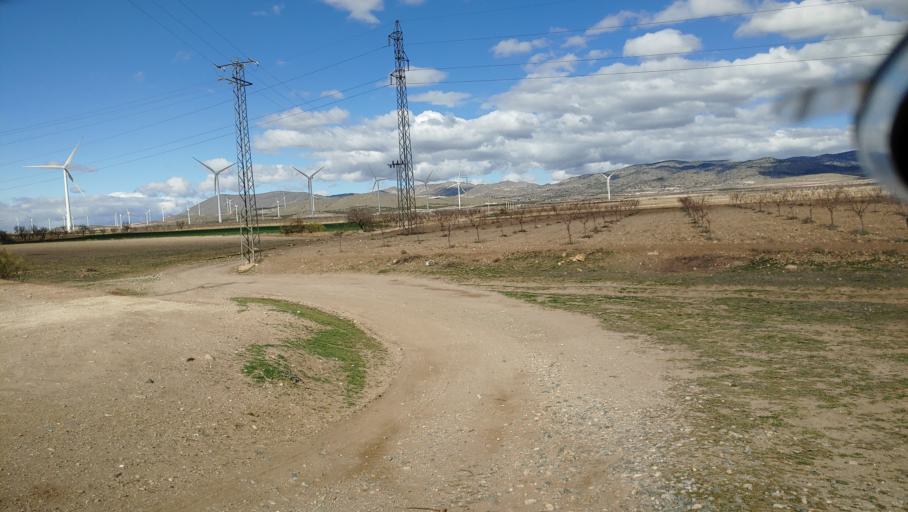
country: ES
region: Andalusia
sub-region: Provincia de Granada
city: Hueneja
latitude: 37.2234
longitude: -2.9525
